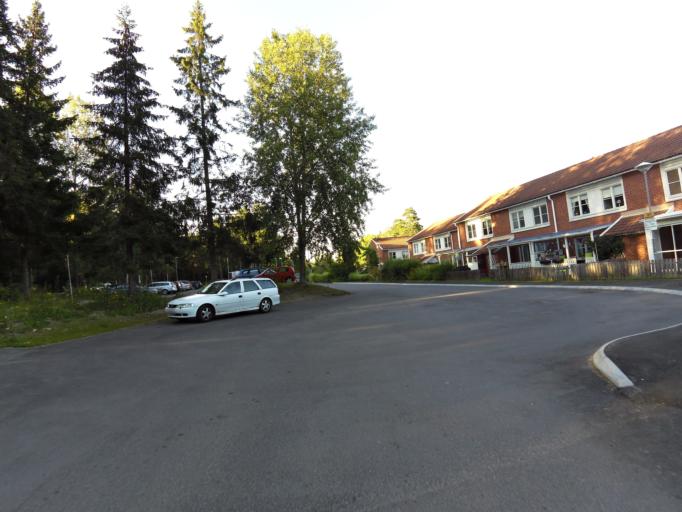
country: SE
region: Gaevleborg
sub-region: Gavle Kommun
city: Gavle
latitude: 60.6489
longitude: 17.1311
